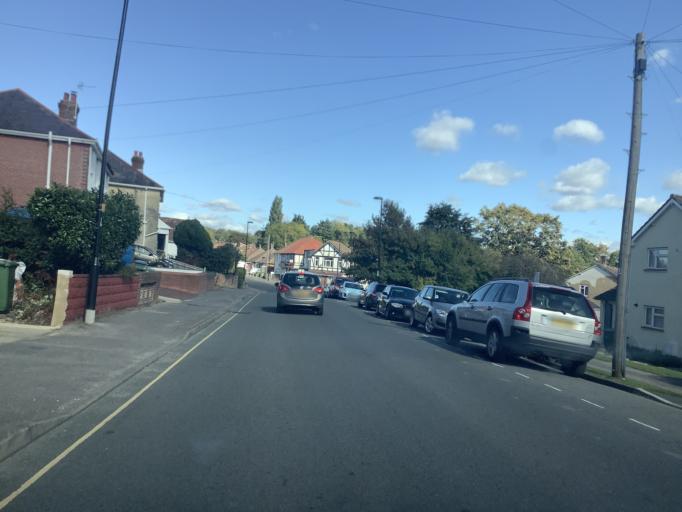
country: GB
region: England
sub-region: Hampshire
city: Marchwood
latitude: 50.9329
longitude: -1.4458
